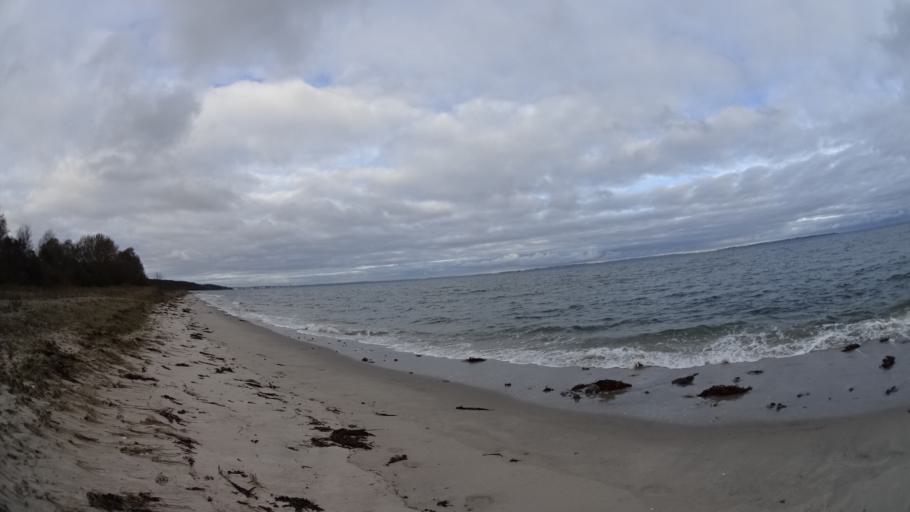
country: DK
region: Central Jutland
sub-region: Arhus Kommune
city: Beder
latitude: 56.0501
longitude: 10.2693
